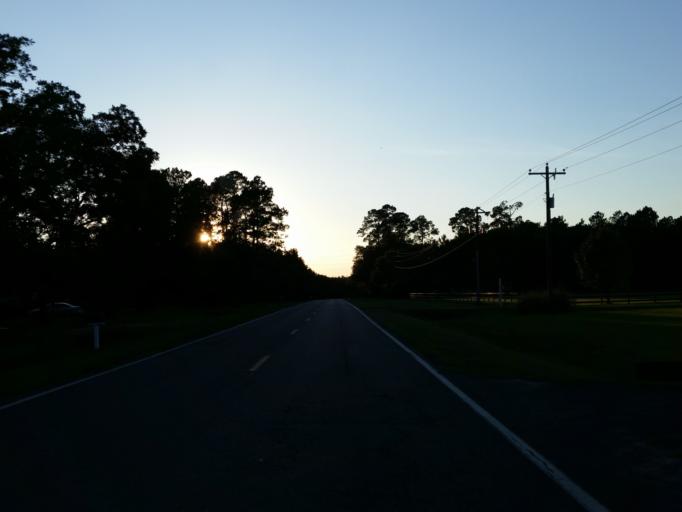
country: US
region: Georgia
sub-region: Berrien County
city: Nashville
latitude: 31.1975
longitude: -83.2223
